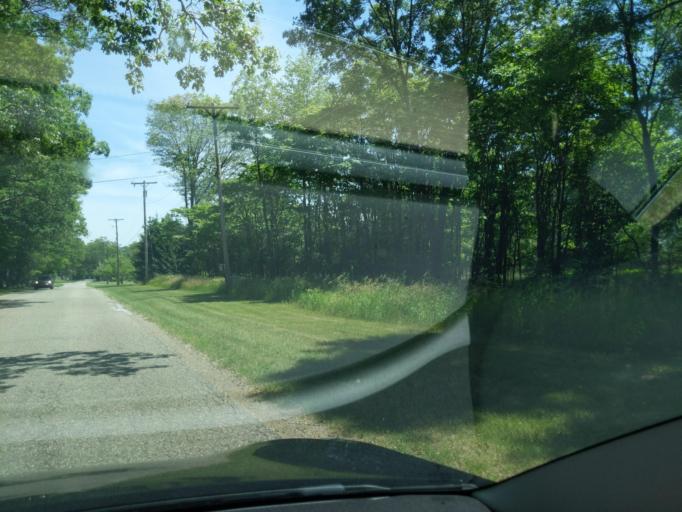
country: US
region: Michigan
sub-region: Muskegon County
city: Montague
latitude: 43.4153
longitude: -86.3695
